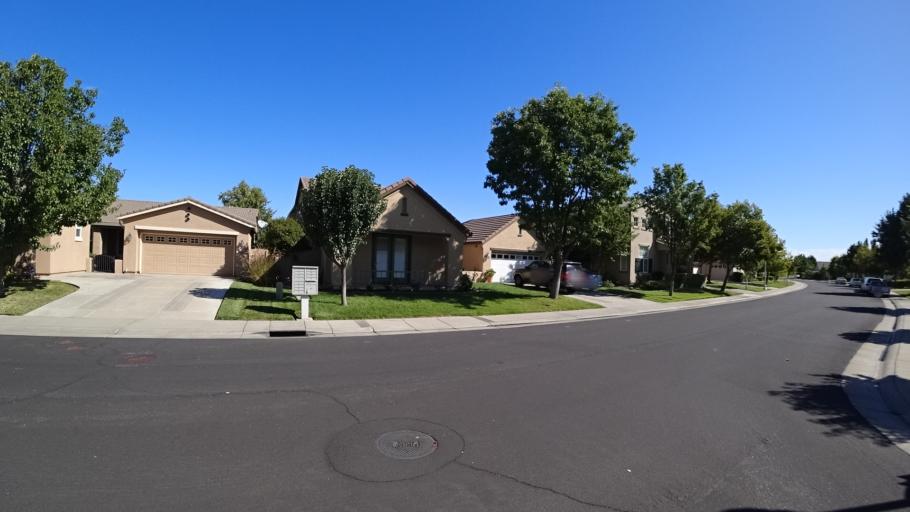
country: US
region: California
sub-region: Sacramento County
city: Laguna
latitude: 38.4236
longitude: -121.4790
